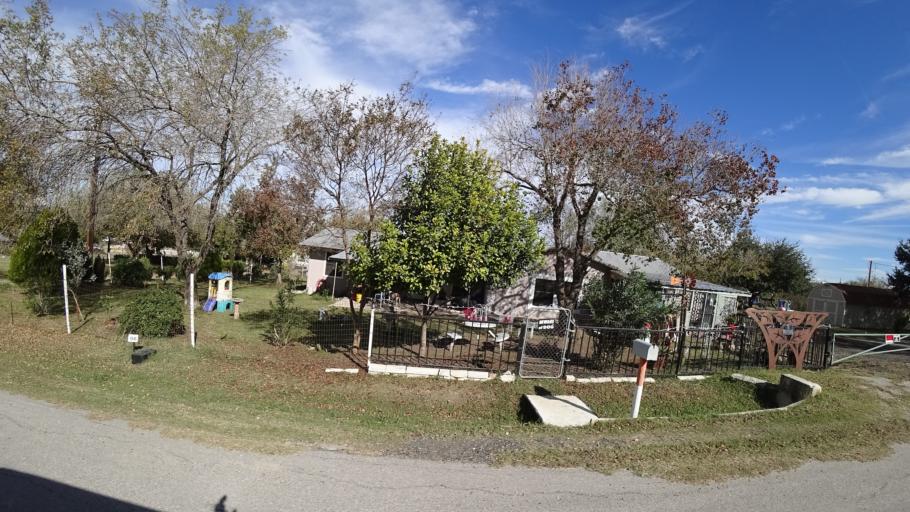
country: US
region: Texas
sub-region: Travis County
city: Onion Creek
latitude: 30.1171
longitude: -97.7003
